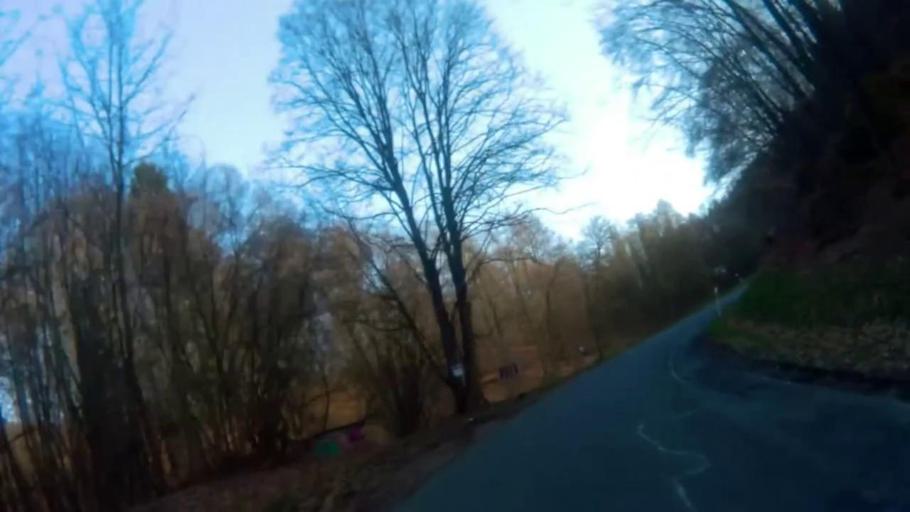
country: DE
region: Hesse
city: Gross-Bieberau
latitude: 49.7602
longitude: 8.8183
